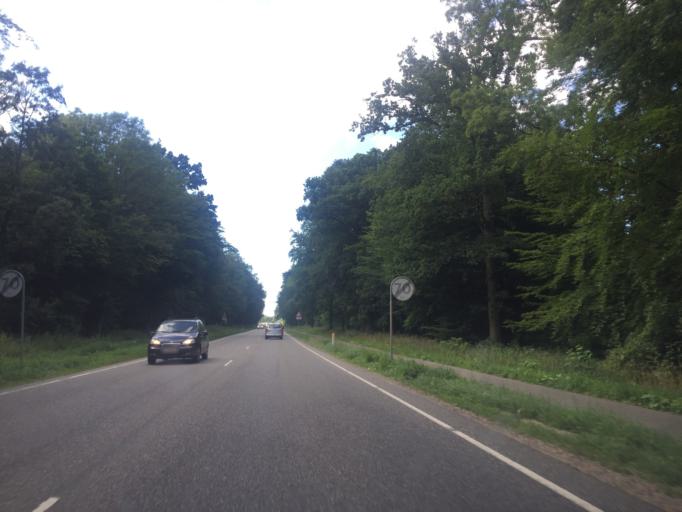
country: DK
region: Zealand
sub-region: Guldborgsund Kommune
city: Nykobing Falster
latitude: 54.7391
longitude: 11.9195
